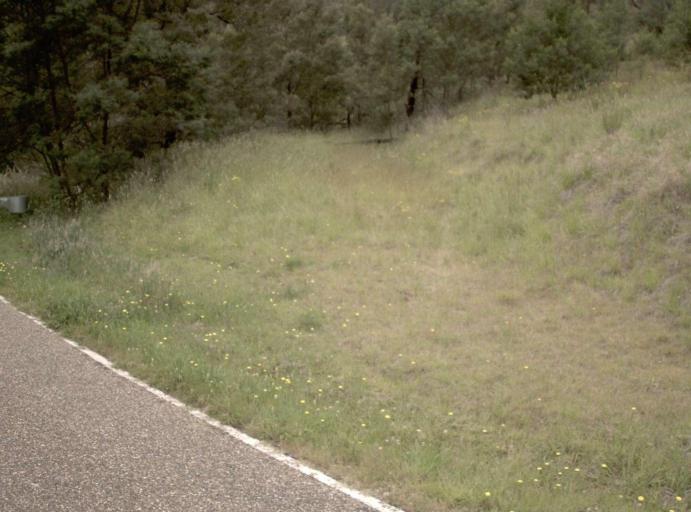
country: AU
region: Victoria
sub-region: East Gippsland
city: Bairnsdale
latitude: -37.5434
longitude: 147.2037
